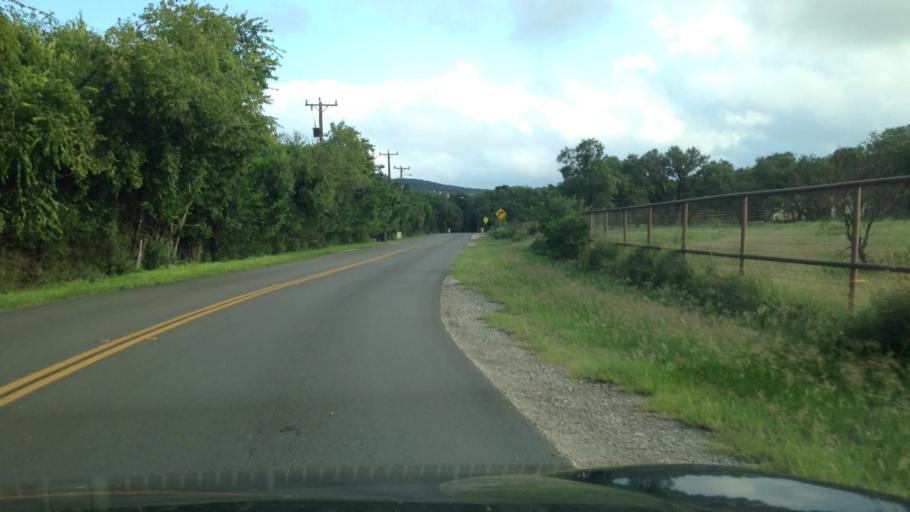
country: US
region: Texas
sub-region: Bexar County
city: Cross Mountain
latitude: 29.6336
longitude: -98.6027
